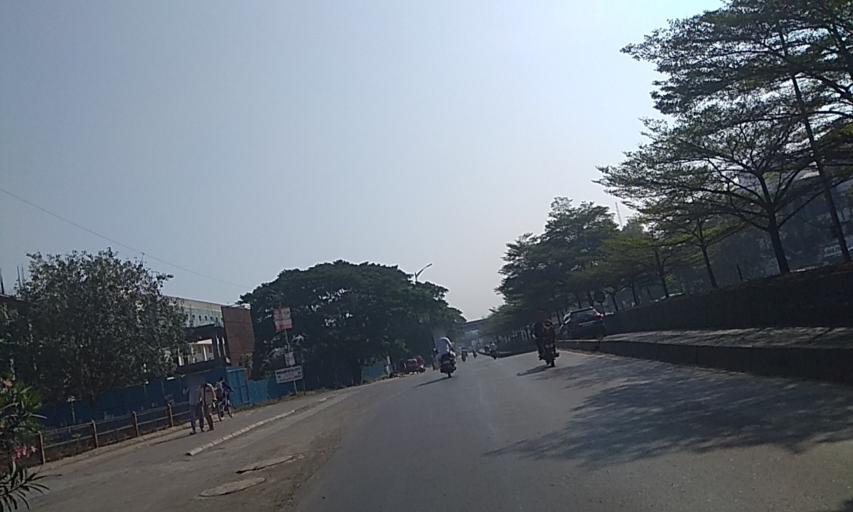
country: IN
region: Maharashtra
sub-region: Pune Division
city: Pune
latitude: 18.5034
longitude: 73.9243
